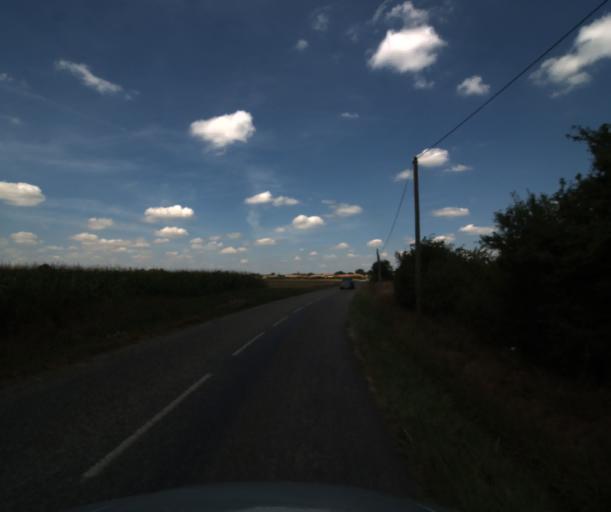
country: FR
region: Midi-Pyrenees
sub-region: Departement de la Haute-Garonne
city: Saint-Lys
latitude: 43.5000
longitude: 1.1763
